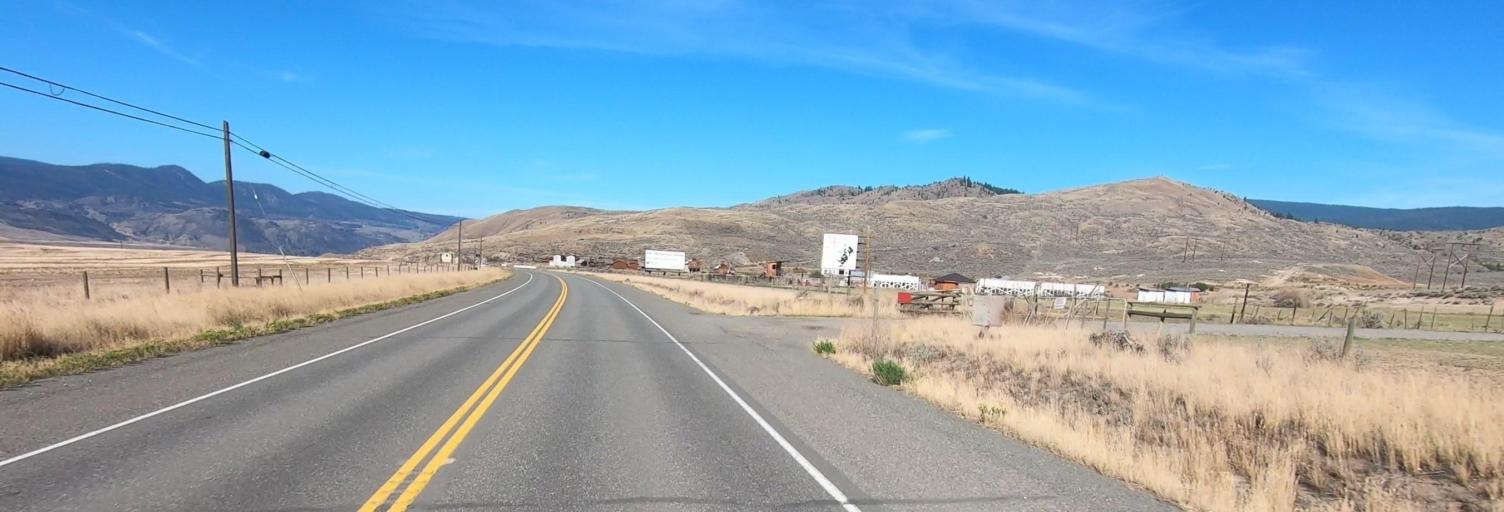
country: CA
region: British Columbia
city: Logan Lake
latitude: 50.7719
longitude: -120.9478
